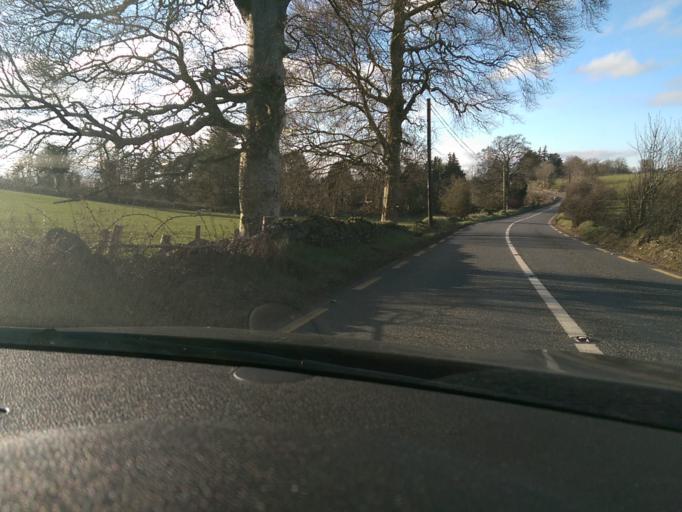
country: IE
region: Connaught
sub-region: Roscommon
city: Roscommon
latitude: 53.7600
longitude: -8.2440
